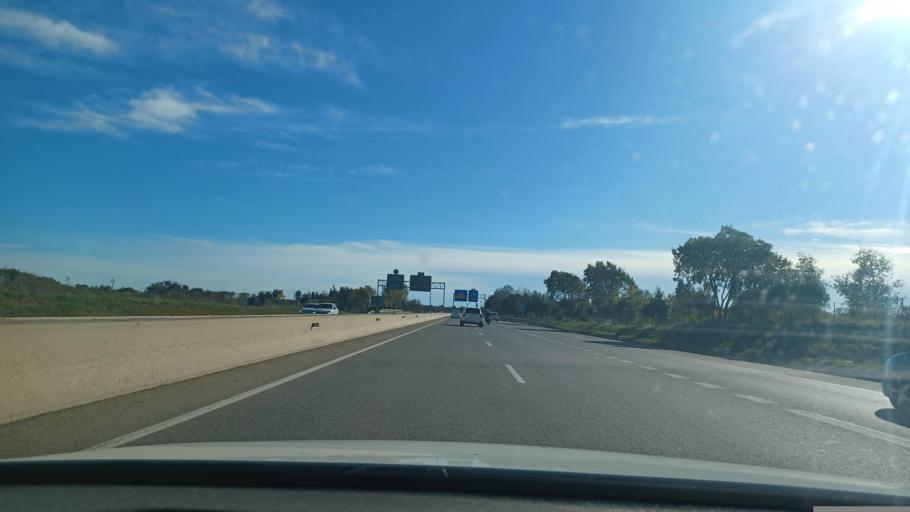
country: ES
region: Catalonia
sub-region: Provincia de Tarragona
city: Vila-seca
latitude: 41.1434
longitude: 1.1408
